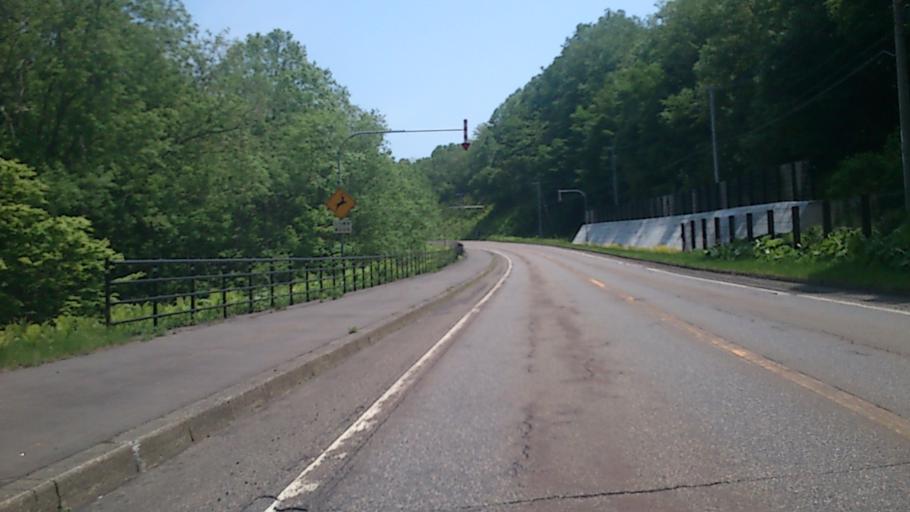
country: JP
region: Hokkaido
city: Otofuke
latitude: 43.3621
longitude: 143.2462
